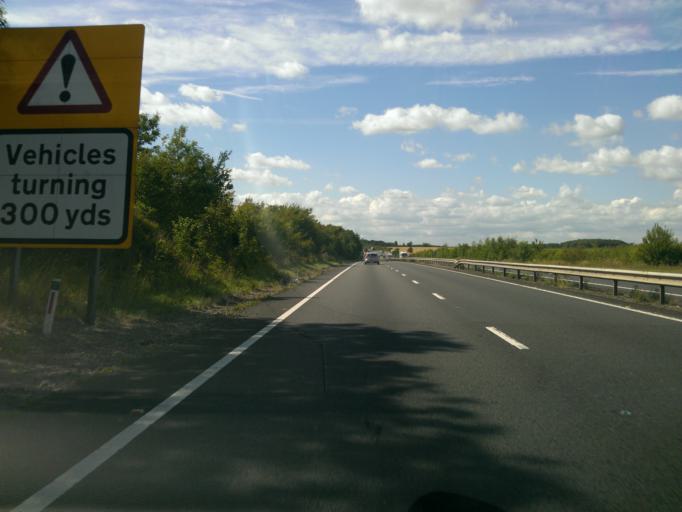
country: GB
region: England
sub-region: Northamptonshire
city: Thrapston
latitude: 52.3758
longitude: -0.4672
